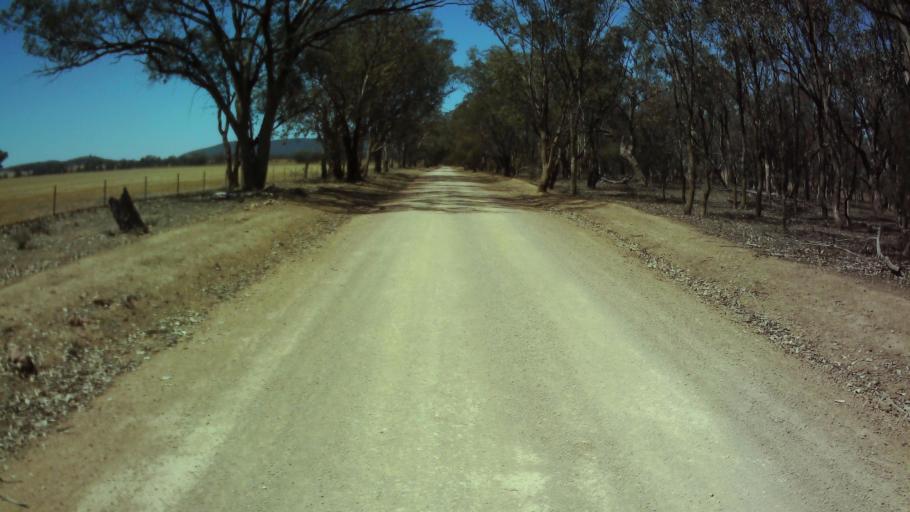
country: AU
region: New South Wales
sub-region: Weddin
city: Grenfell
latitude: -33.9191
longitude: 148.0789
